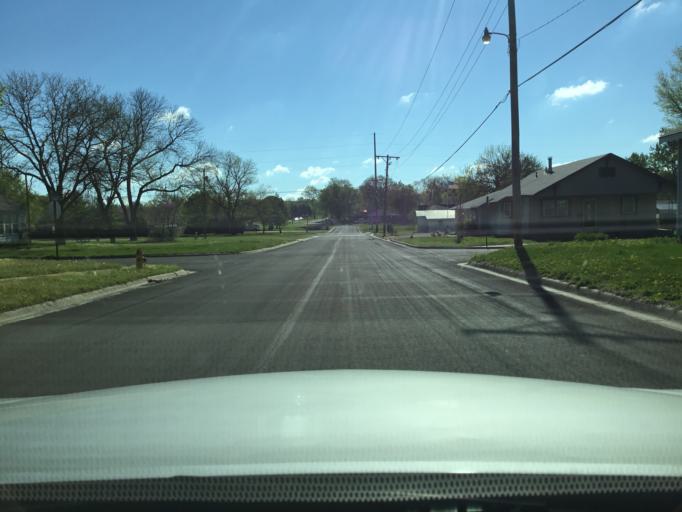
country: US
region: Kansas
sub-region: Allen County
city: Iola
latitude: 37.9333
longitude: -95.4013
